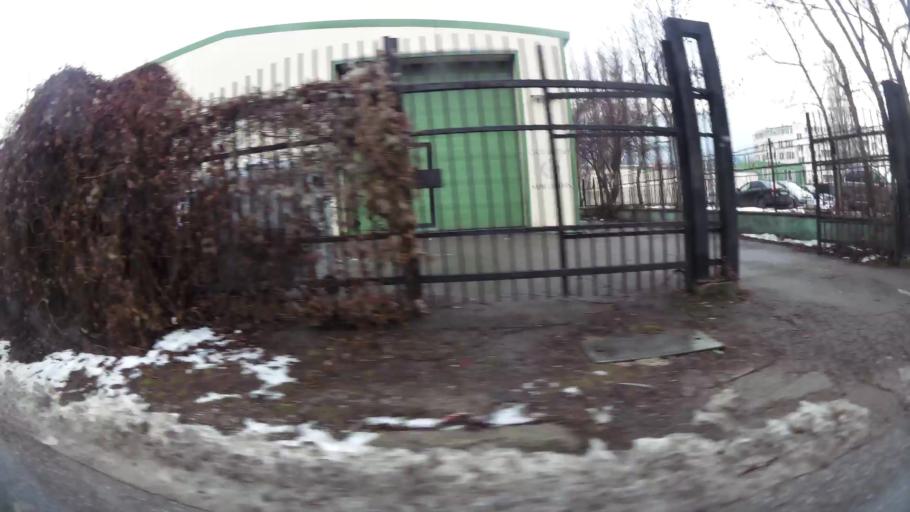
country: BG
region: Sofia-Capital
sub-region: Stolichna Obshtina
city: Sofia
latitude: 42.6659
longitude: 23.2519
